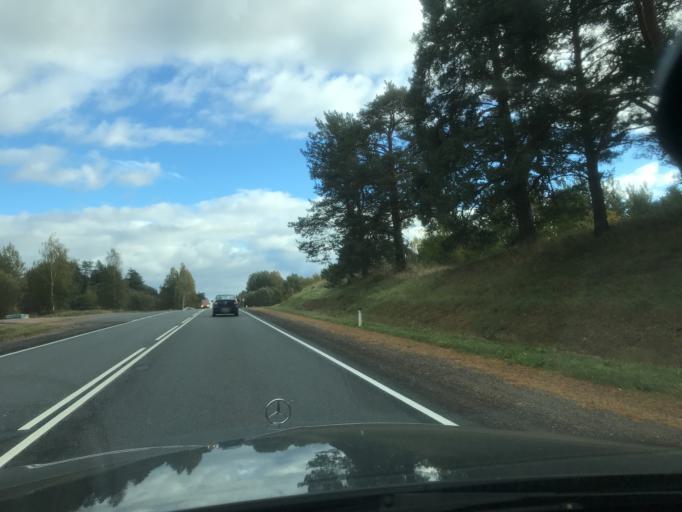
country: RU
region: Pskov
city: Opochka
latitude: 56.6585
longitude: 28.7516
